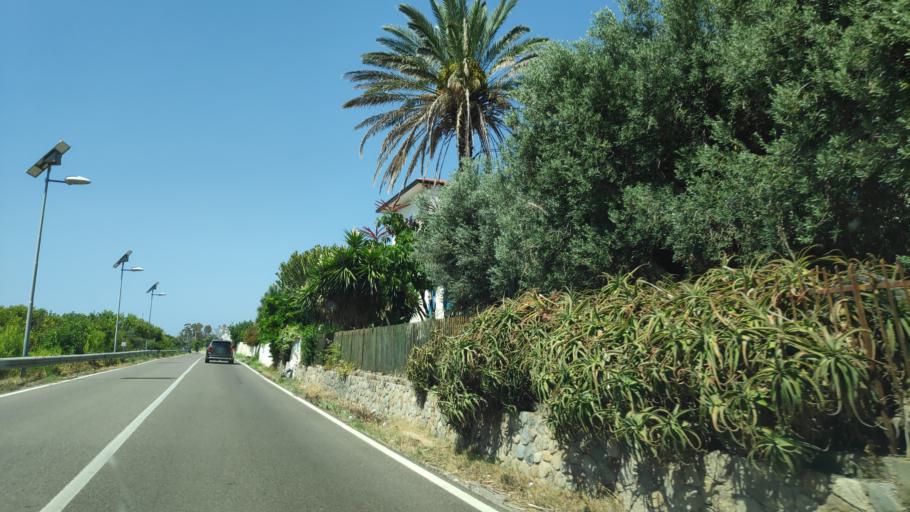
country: IT
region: Calabria
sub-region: Provincia di Reggio Calabria
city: Weather Station
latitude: 37.9243
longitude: 16.0498
